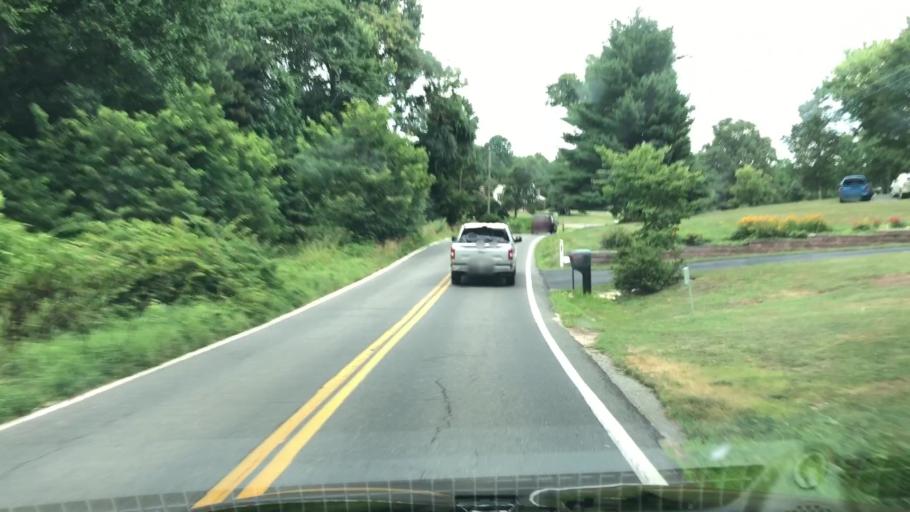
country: US
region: Virginia
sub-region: Stafford County
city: Falmouth
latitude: 38.3392
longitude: -77.5090
